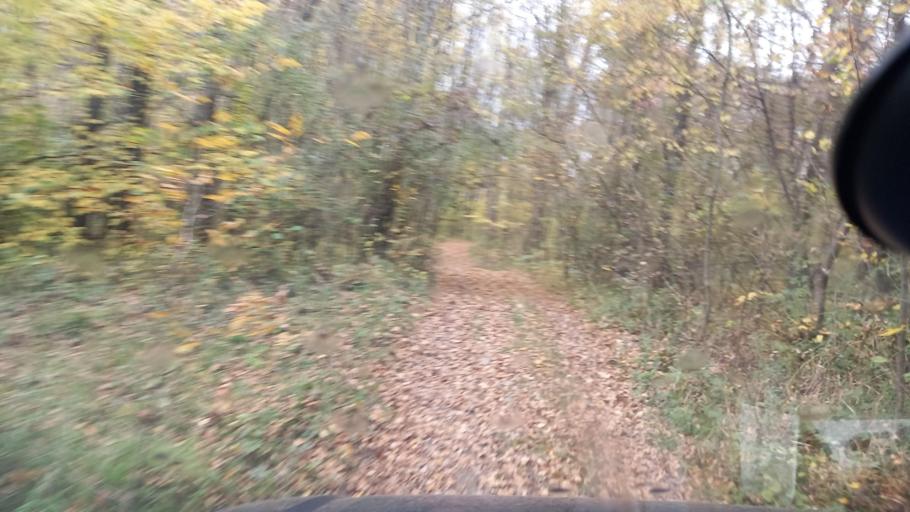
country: RU
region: Krasnodarskiy
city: Shedok
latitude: 44.1707
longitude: 40.8464
